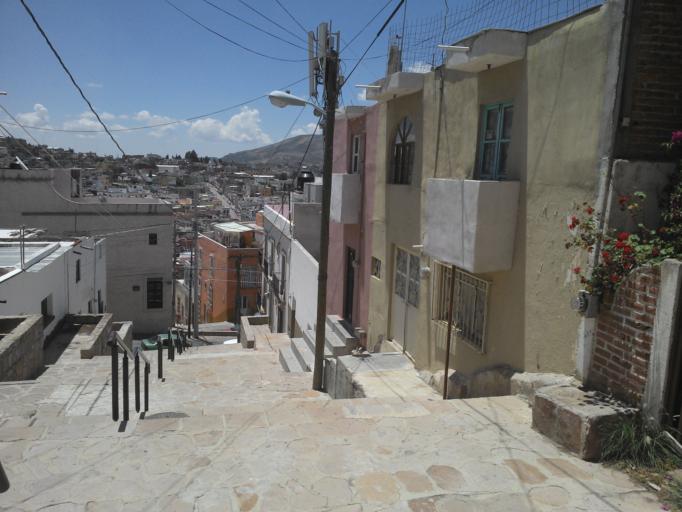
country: MX
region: Zacatecas
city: Zacatecas
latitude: 22.7781
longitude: -102.5734
